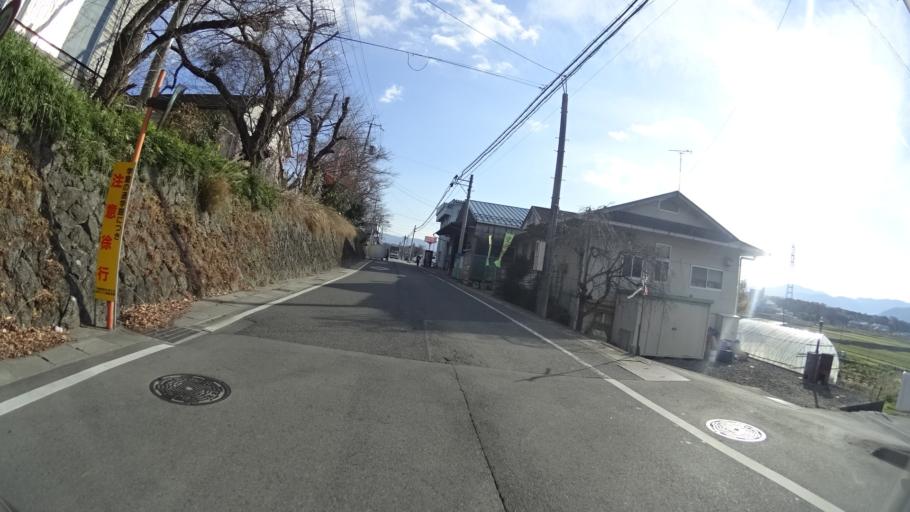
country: JP
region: Kyoto
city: Kameoka
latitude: 35.0528
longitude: 135.5796
